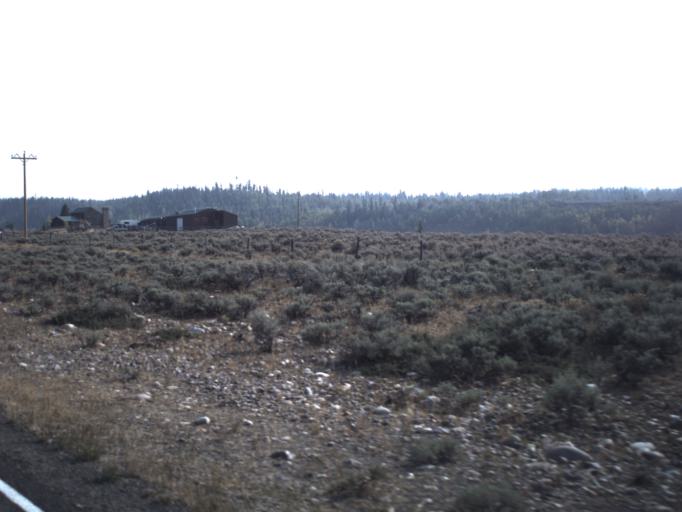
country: US
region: Wyoming
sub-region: Uinta County
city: Evanston
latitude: 40.9475
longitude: -110.8398
